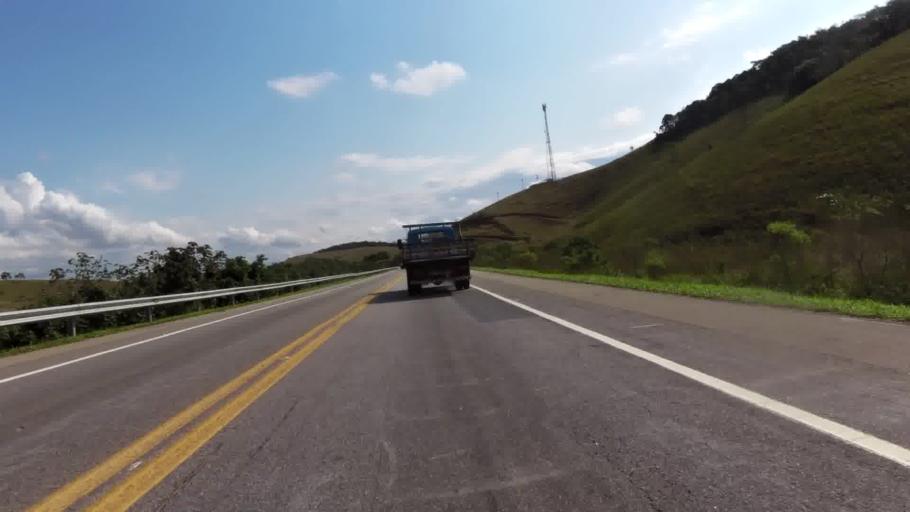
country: BR
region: Rio de Janeiro
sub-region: Macae
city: Macae
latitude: -22.2435
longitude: -41.8033
